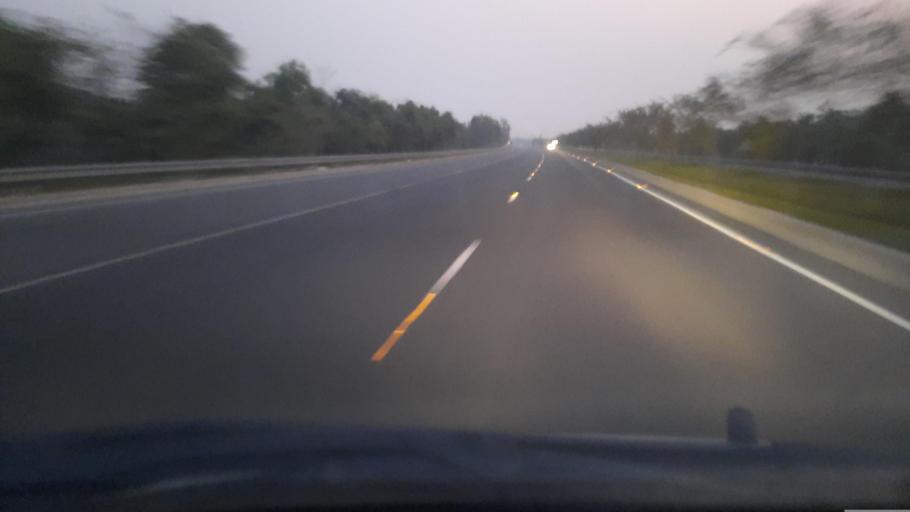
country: BD
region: Dhaka
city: Char Bhadrasan
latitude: 23.4012
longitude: 90.2459
